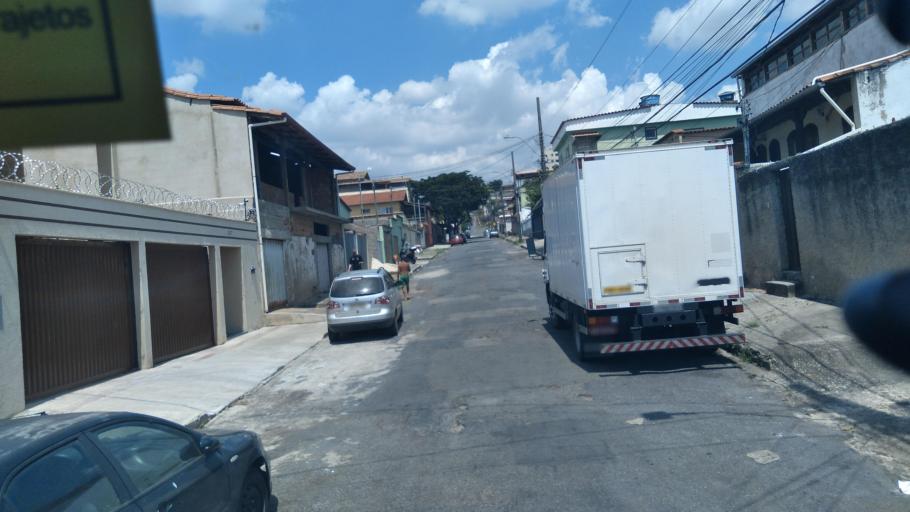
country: BR
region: Minas Gerais
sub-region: Contagem
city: Contagem
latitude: -19.9108
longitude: -44.0034
